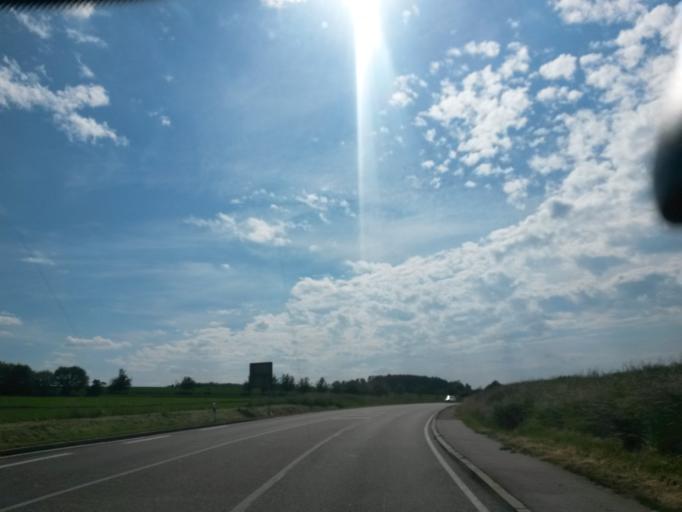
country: DE
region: Baden-Wuerttemberg
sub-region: Regierungsbezirk Stuttgart
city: Renningen
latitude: 48.7494
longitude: 8.9118
